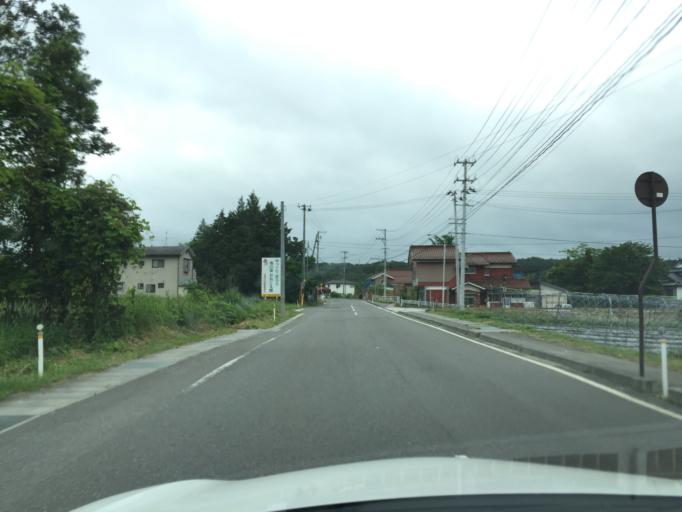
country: JP
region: Fukushima
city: Funehikimachi-funehiki
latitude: 37.4131
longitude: 140.6096
